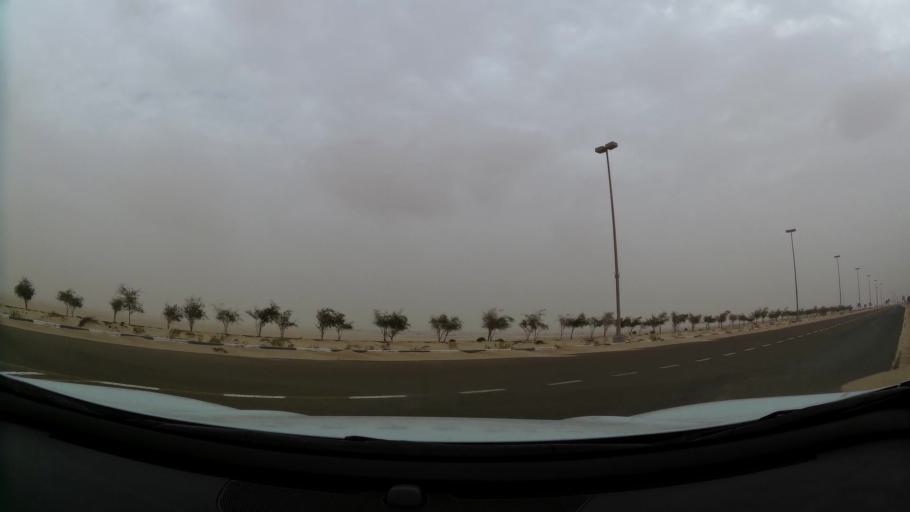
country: AE
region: Abu Dhabi
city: Abu Dhabi
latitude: 24.4251
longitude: 54.7086
